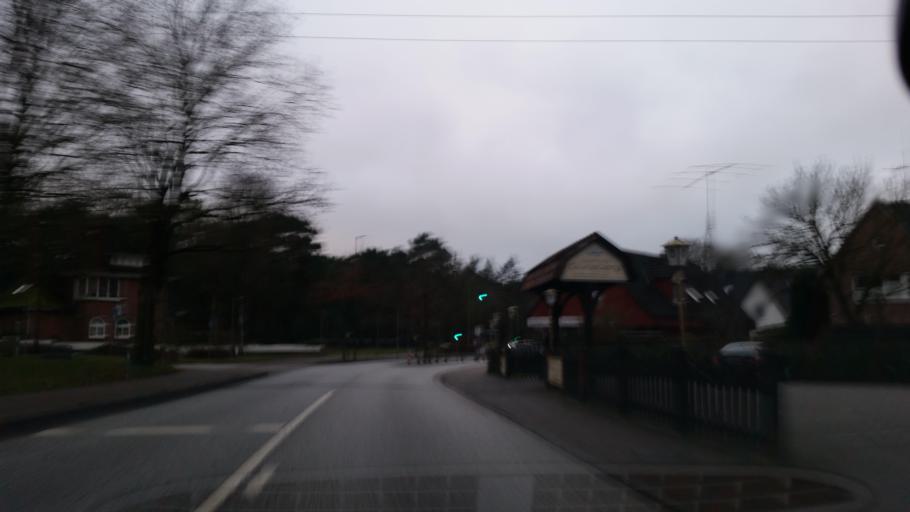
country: DE
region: Schleswig-Holstein
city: Geesthacht
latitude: 53.4408
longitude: 10.3590
